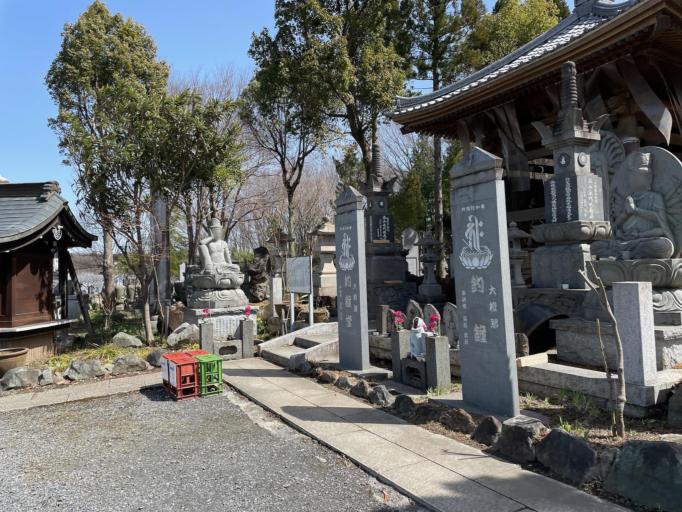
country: JP
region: Saitama
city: Ogawa
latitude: 36.0260
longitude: 139.3319
